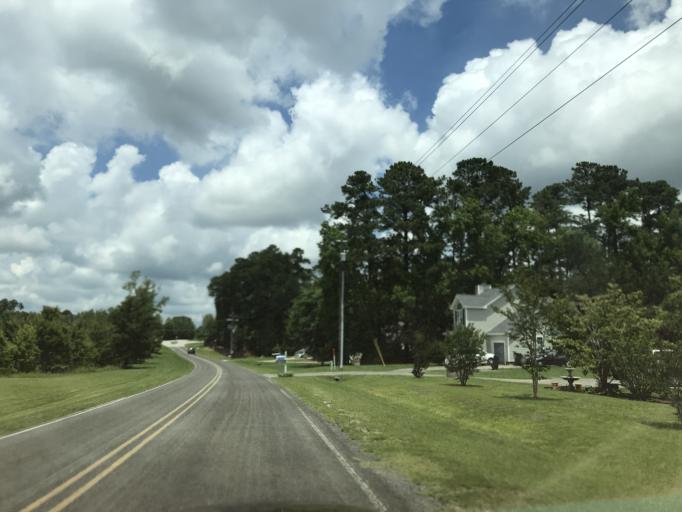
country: US
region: North Carolina
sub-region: Wake County
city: Rolesville
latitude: 35.9505
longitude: -78.3720
